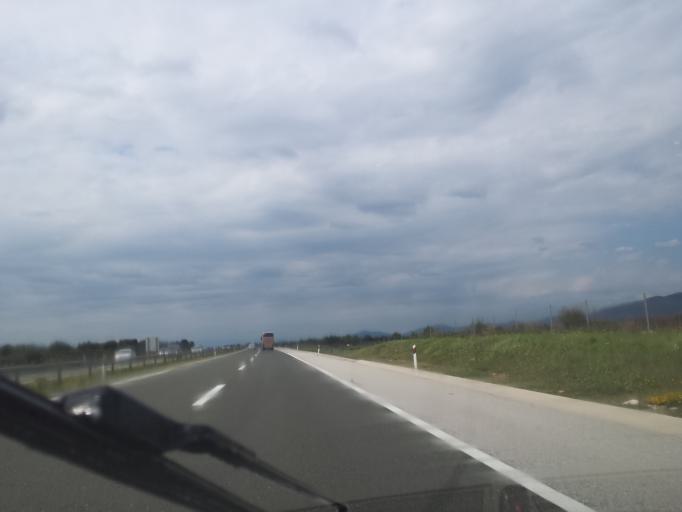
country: HR
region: Licko-Senjska
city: Gospic
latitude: 44.4703
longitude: 15.5906
